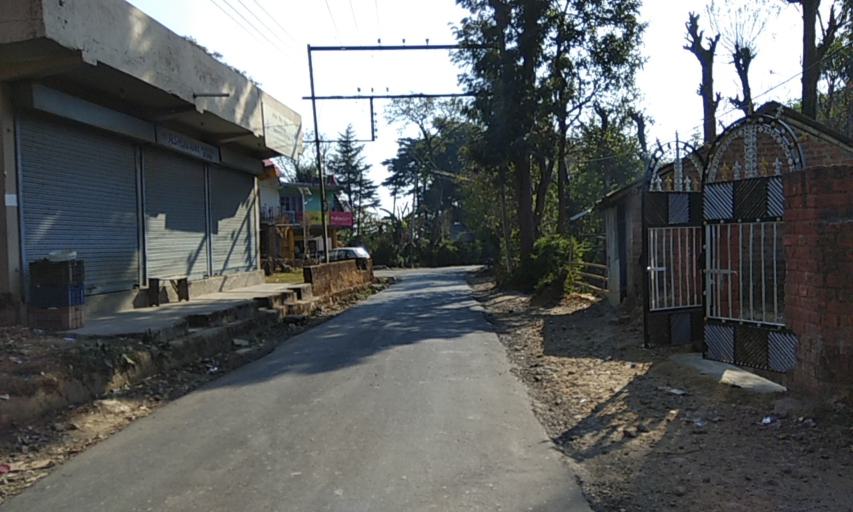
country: IN
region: Himachal Pradesh
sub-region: Kangra
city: Palampur
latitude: 32.1162
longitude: 76.5253
